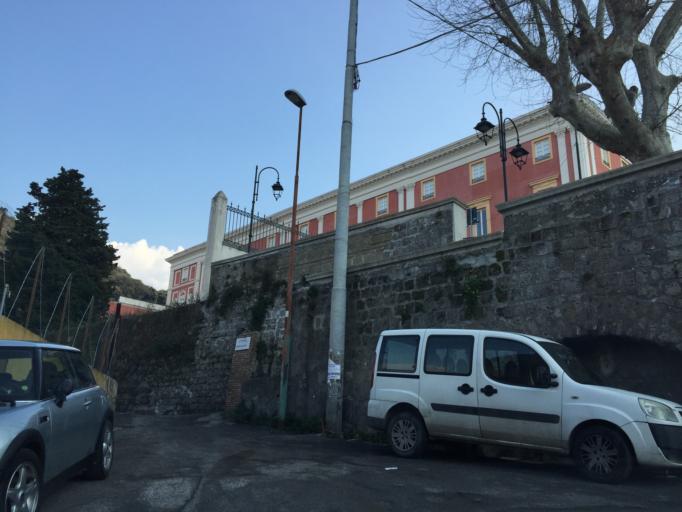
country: IT
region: Campania
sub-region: Provincia di Napoli
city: Piazza-Tralia-Pendolo
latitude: 40.6855
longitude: 14.4885
